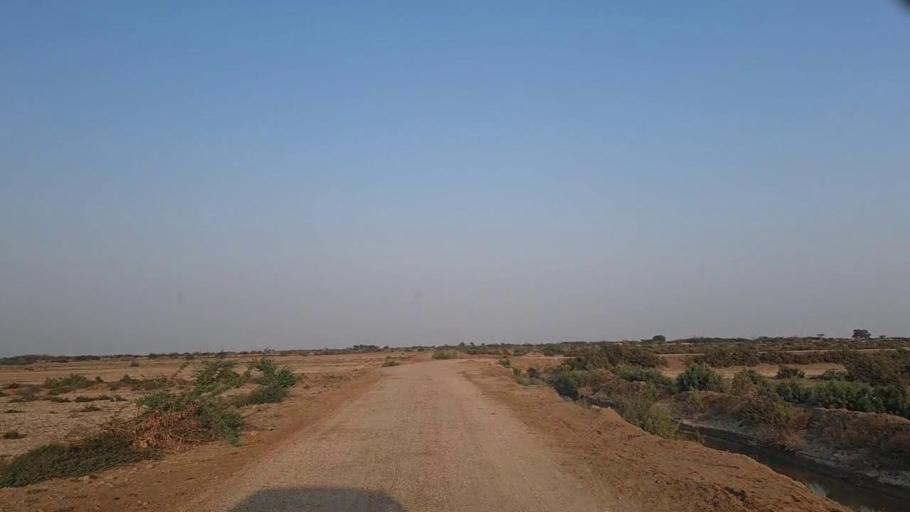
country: PK
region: Sindh
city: Jati
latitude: 24.4889
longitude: 68.4145
